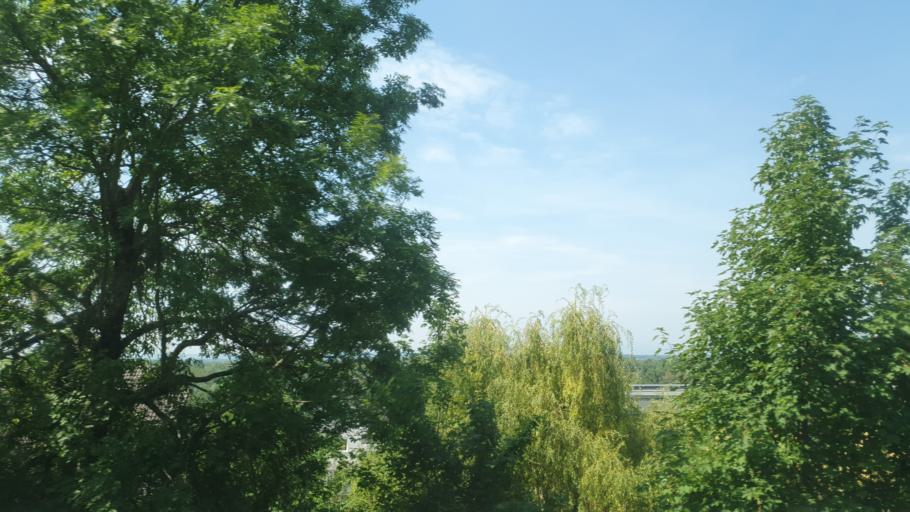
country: DE
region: Baden-Wuerttemberg
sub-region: Freiburg Region
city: Bad Bellingen
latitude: 47.7367
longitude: 7.5561
